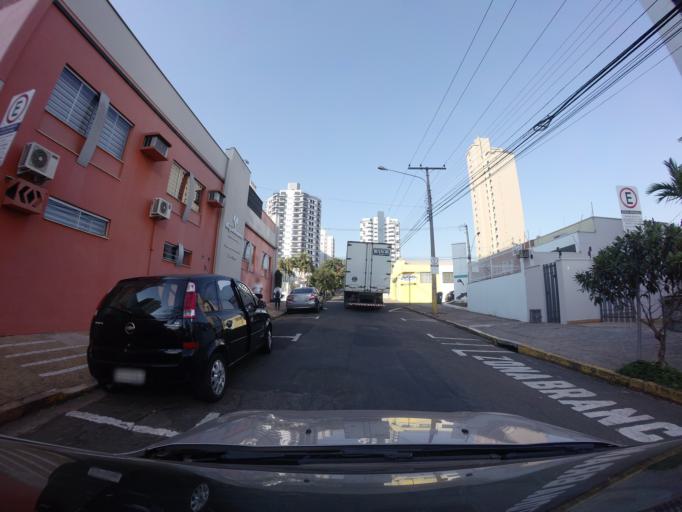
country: BR
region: Sao Paulo
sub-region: Piracicaba
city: Piracicaba
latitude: -22.7300
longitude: -47.6546
